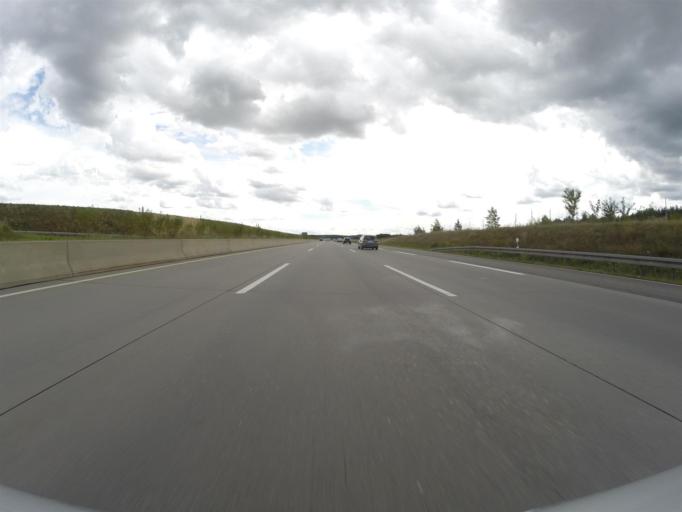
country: DE
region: Thuringia
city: Tautendorf
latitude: 50.8056
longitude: 11.8954
